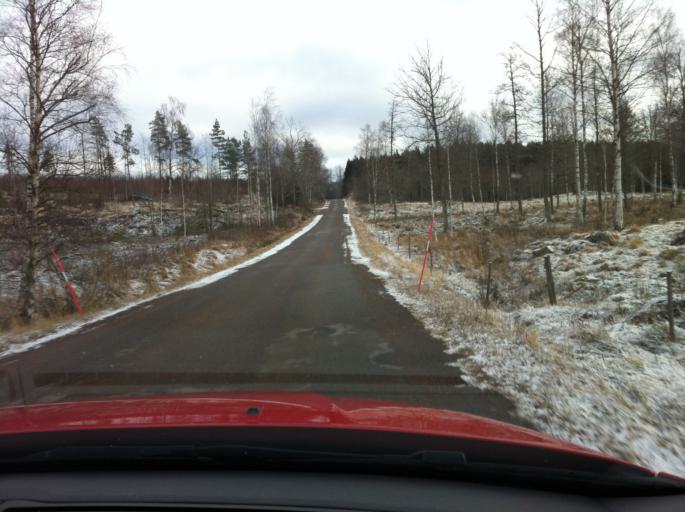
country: SE
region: Joenkoeping
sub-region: Eksjo Kommun
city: Mariannelund
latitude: 57.6135
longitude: 15.6740
